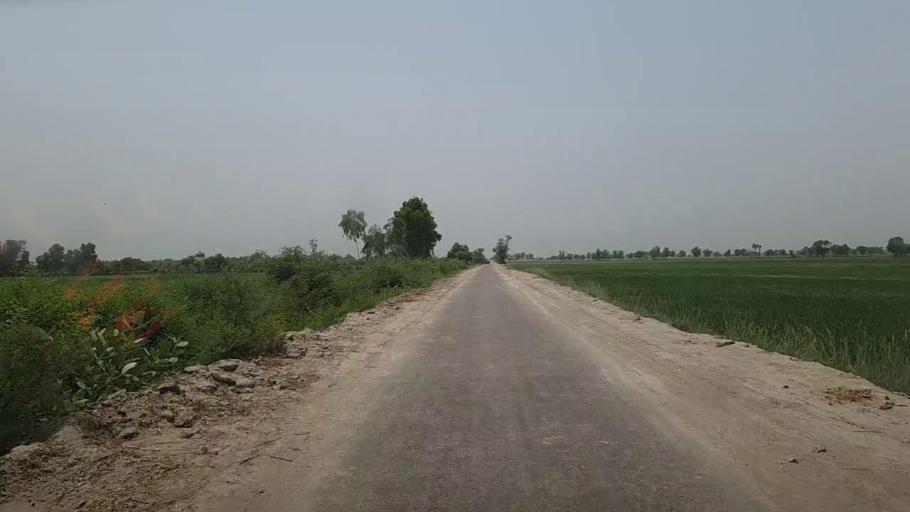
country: PK
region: Sindh
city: Sita Road
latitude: 27.0709
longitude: 67.9062
